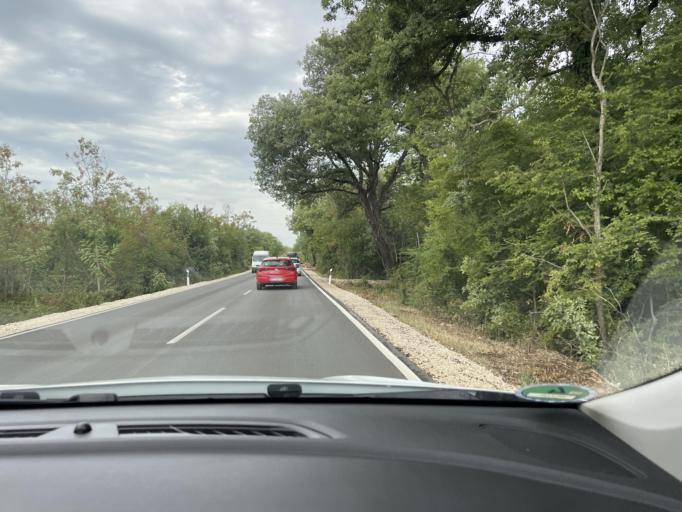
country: HR
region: Istarska
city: Vrsar
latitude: 45.1826
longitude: 13.7293
